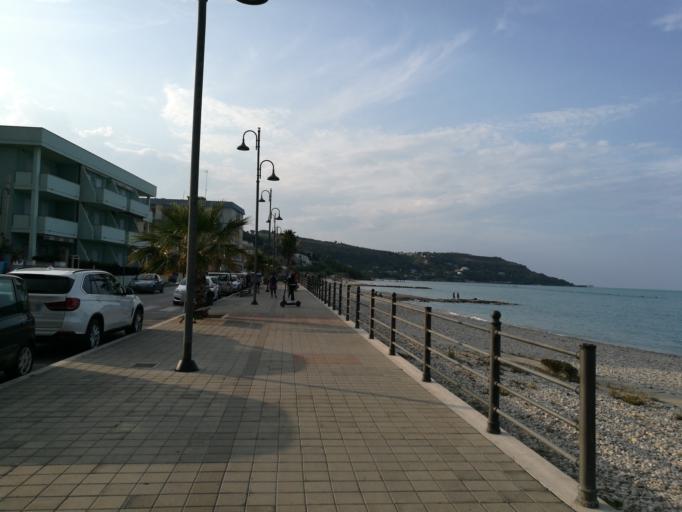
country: IT
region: Abruzzo
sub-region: Provincia di Chieti
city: Fossacesia
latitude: 42.2513
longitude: 14.5098
